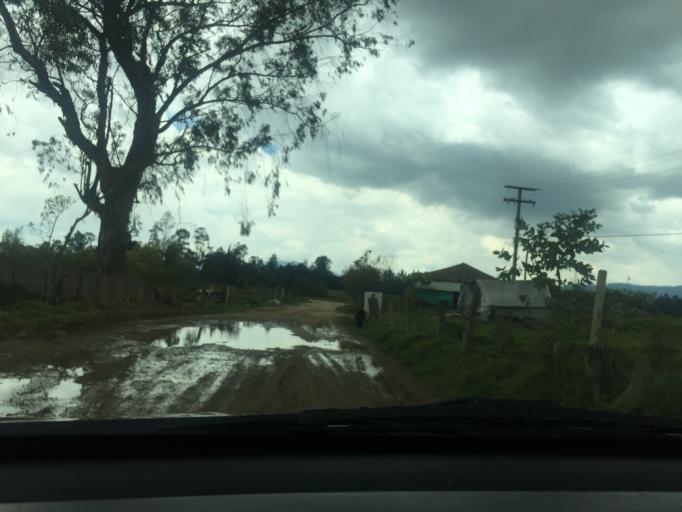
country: CO
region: Cundinamarca
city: Madrid
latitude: 4.7870
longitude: -74.2789
